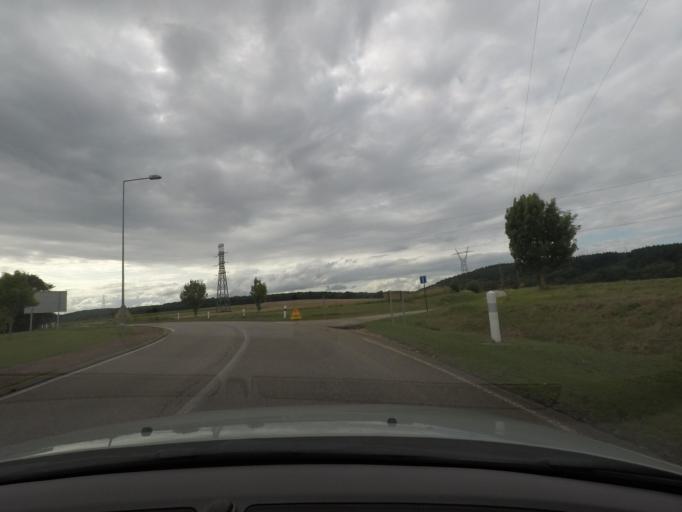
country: FR
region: Haute-Normandie
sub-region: Departement de l'Eure
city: Le Manoir
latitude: 49.3271
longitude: 1.2176
